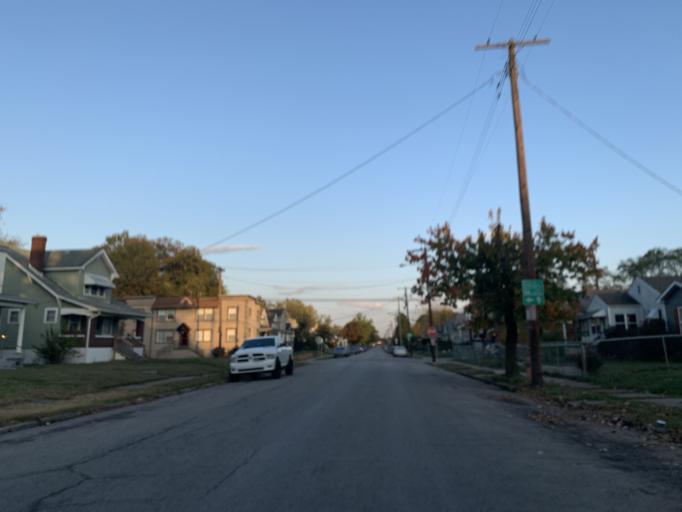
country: US
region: Indiana
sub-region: Floyd County
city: New Albany
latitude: 38.2564
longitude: -85.8146
